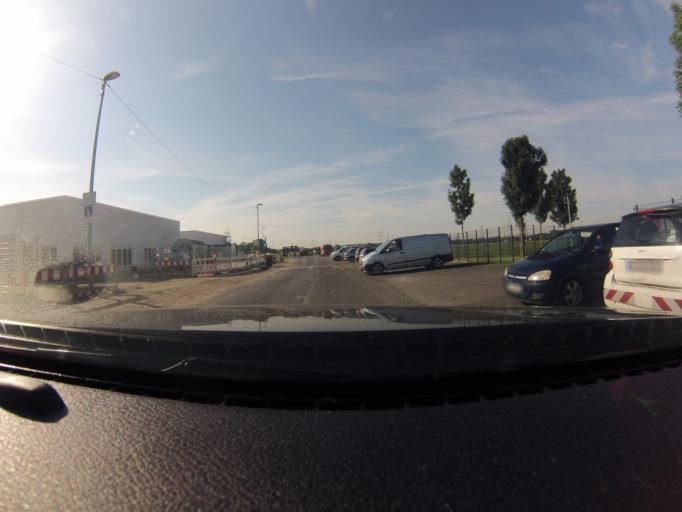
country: DE
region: North Rhine-Westphalia
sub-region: Regierungsbezirk Koln
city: Frechen
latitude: 50.9121
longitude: 6.8545
